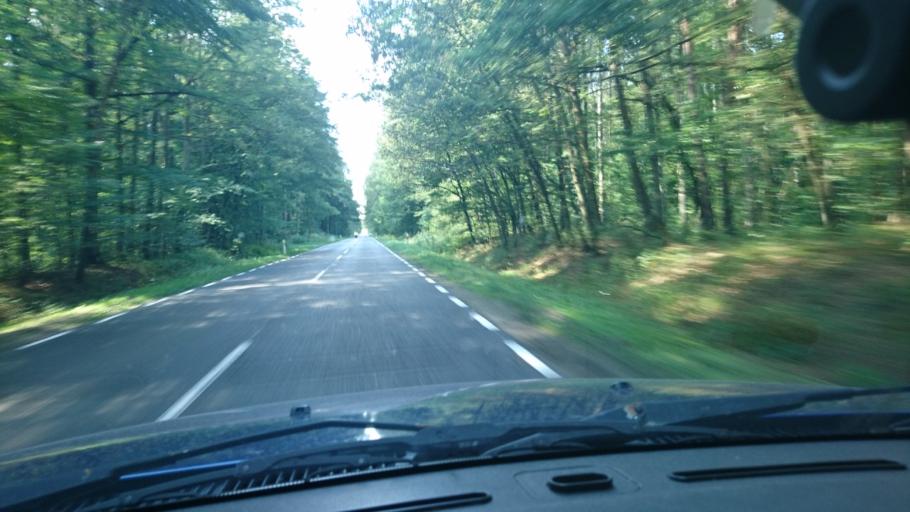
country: PL
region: Greater Poland Voivodeship
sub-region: Powiat ostrowski
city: Odolanow
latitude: 51.5980
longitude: 17.6058
